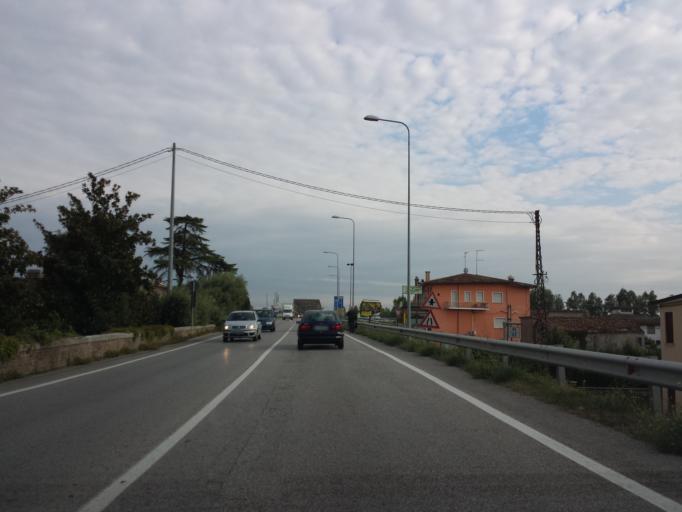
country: IT
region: Veneto
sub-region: Provincia di Padova
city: Boara Pisani
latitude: 45.1072
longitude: 11.7822
